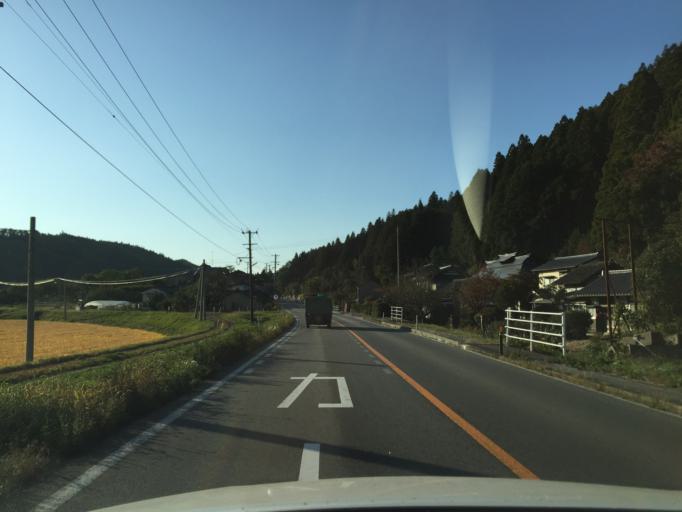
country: JP
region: Fukushima
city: Iwaki
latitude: 37.1111
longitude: 140.7617
